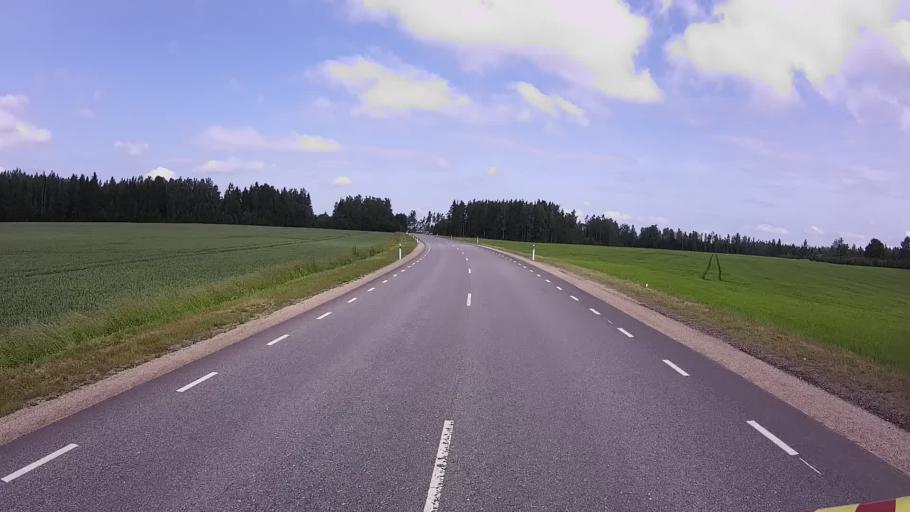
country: EE
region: Polvamaa
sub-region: Polva linn
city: Polva
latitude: 58.1301
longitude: 26.9559
